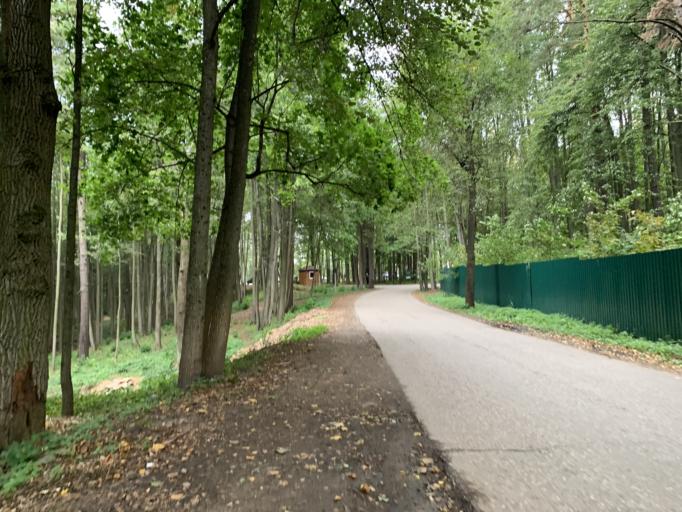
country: RU
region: Moskovskaya
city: Zvenigorod
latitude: 55.7319
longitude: 36.8123
